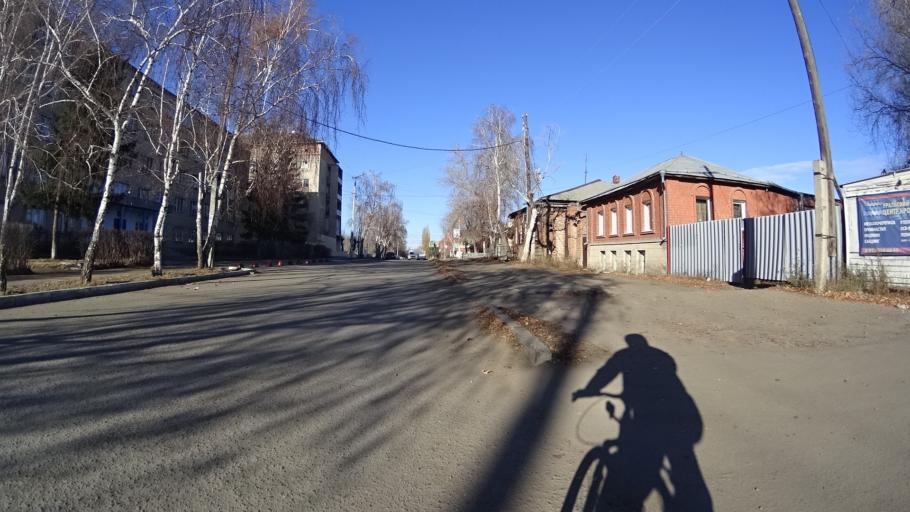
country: RU
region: Chelyabinsk
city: Troitsk
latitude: 54.0839
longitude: 61.5471
